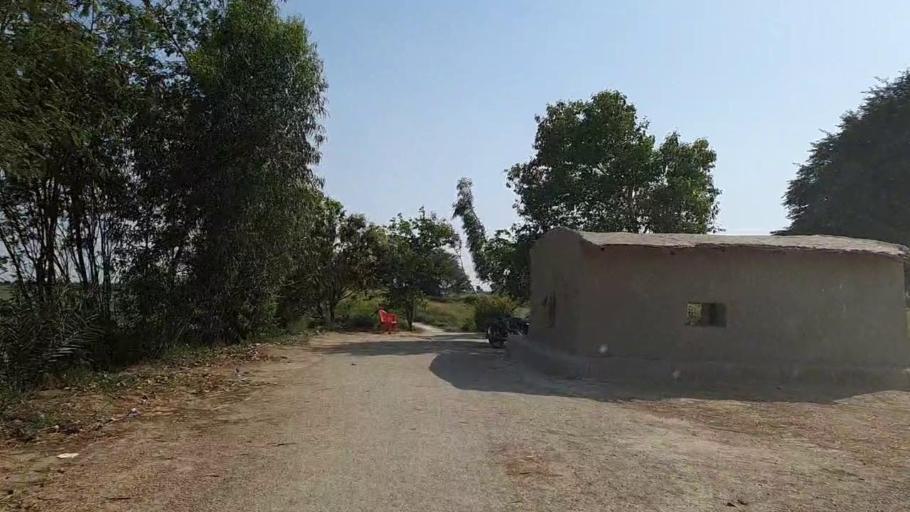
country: PK
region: Sindh
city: Daro Mehar
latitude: 24.7506
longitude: 68.1822
